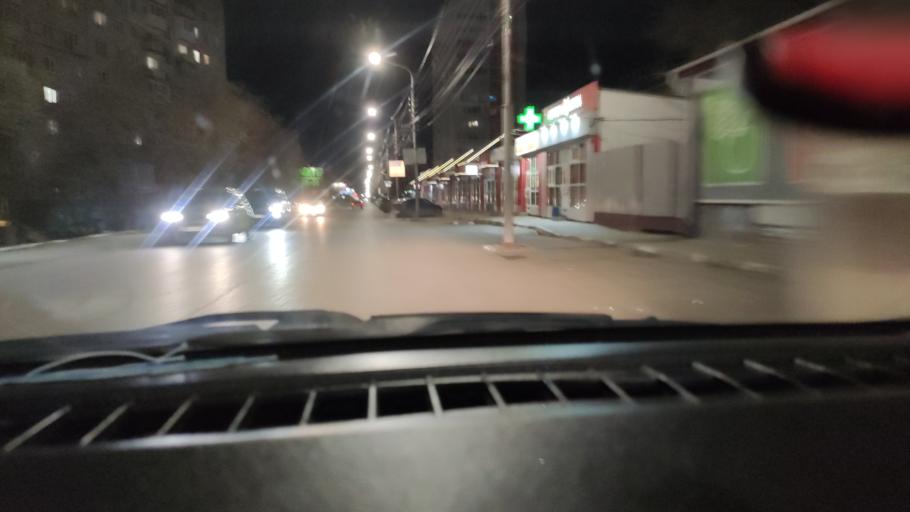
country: RU
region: Saratov
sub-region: Saratovskiy Rayon
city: Saratov
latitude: 51.5649
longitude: 46.0188
